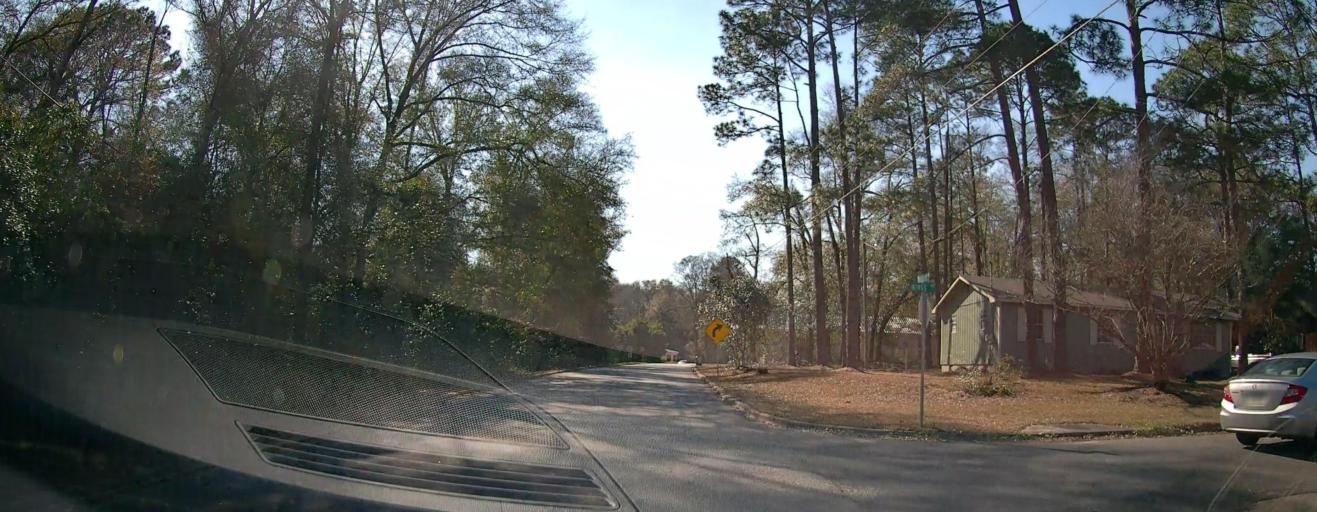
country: US
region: Georgia
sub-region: Macon County
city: Montezuma
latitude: 32.2848
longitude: -84.0235
